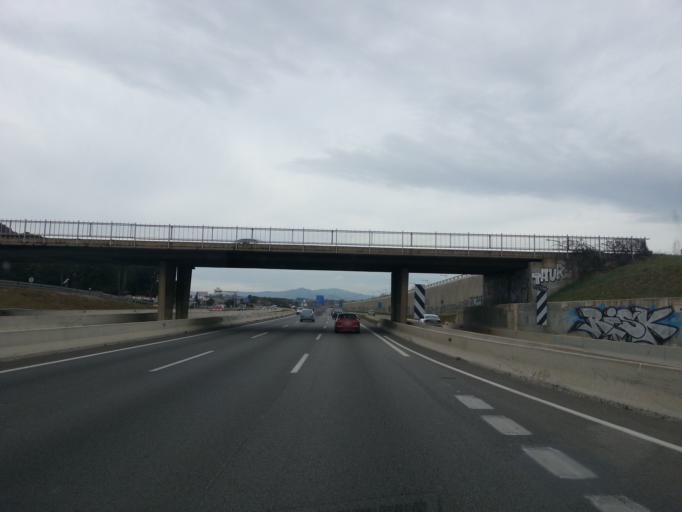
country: ES
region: Catalonia
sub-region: Provincia de Barcelona
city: Sant Quirze del Valles
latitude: 41.5375
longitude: 2.0868
